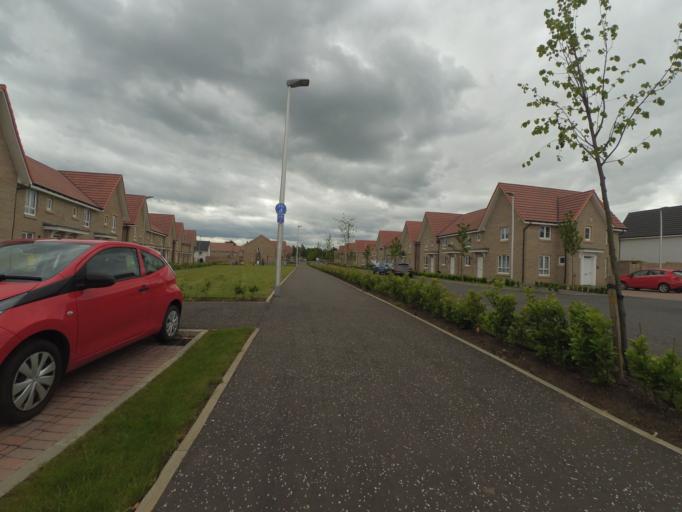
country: GB
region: Scotland
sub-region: East Lothian
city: Musselburgh
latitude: 55.9371
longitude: -3.0911
